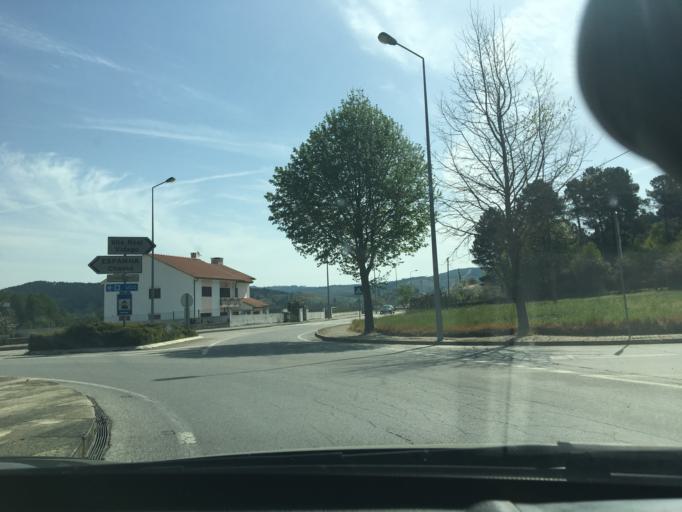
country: PT
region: Vila Real
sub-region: Boticas
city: Boticas
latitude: 41.6860
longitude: -7.6645
